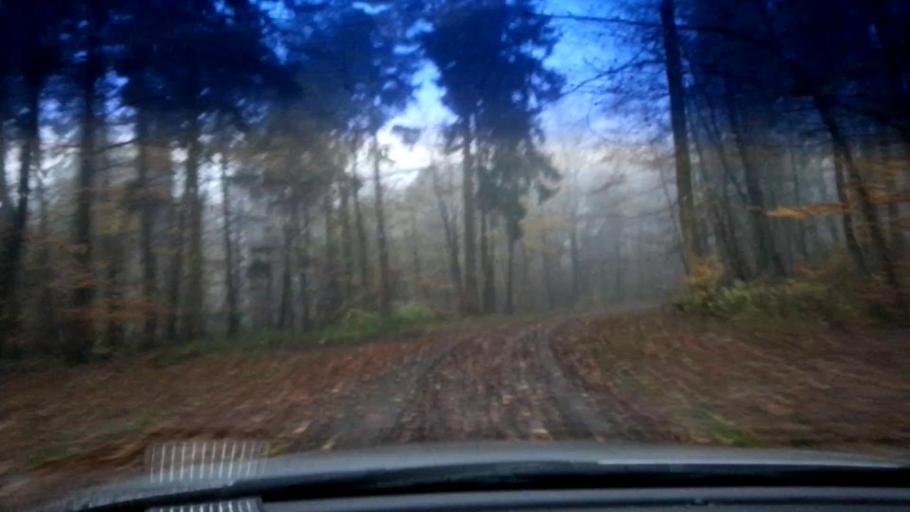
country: DE
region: Bavaria
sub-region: Upper Franconia
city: Schesslitz
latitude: 49.9345
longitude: 11.0594
